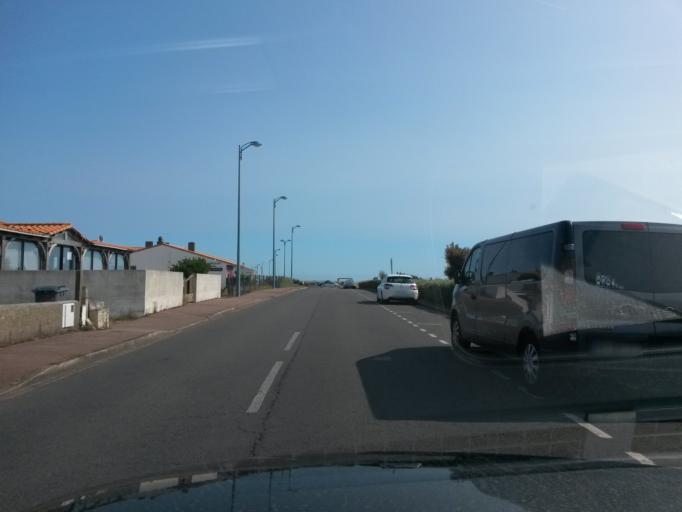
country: FR
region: Pays de la Loire
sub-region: Departement de la Vendee
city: Bretignolles-sur-Mer
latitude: 46.6201
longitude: -1.8722
